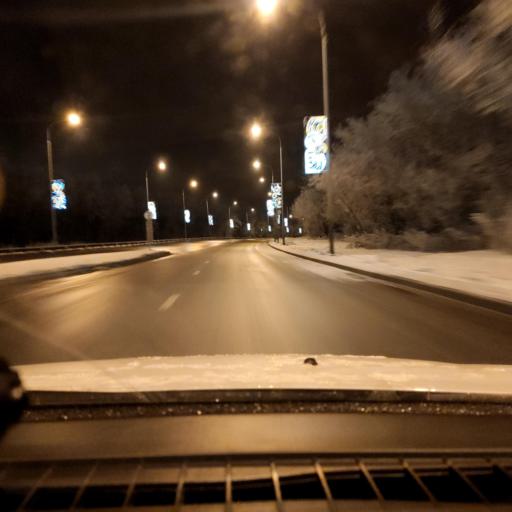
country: RU
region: Samara
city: Petra-Dubrava
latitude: 53.2800
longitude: 50.2531
